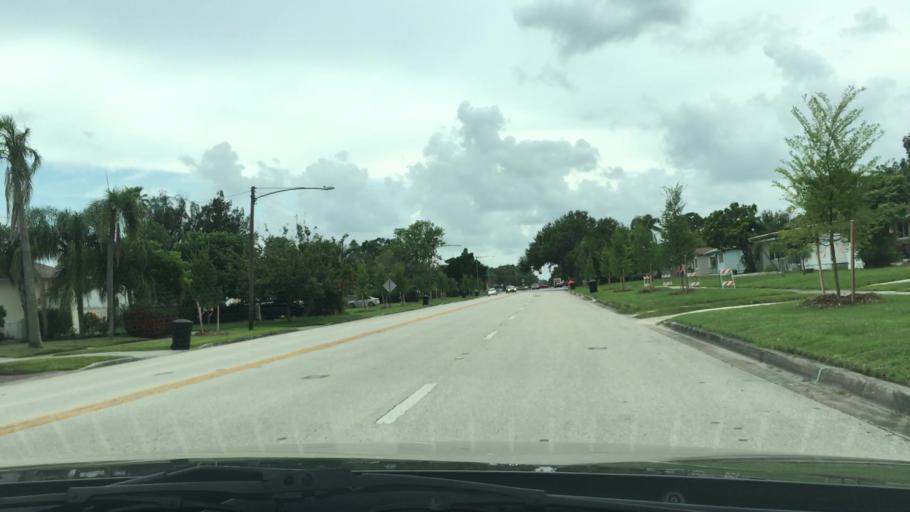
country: US
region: Florida
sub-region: Pinellas County
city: Gandy
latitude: 27.8476
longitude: -82.6356
